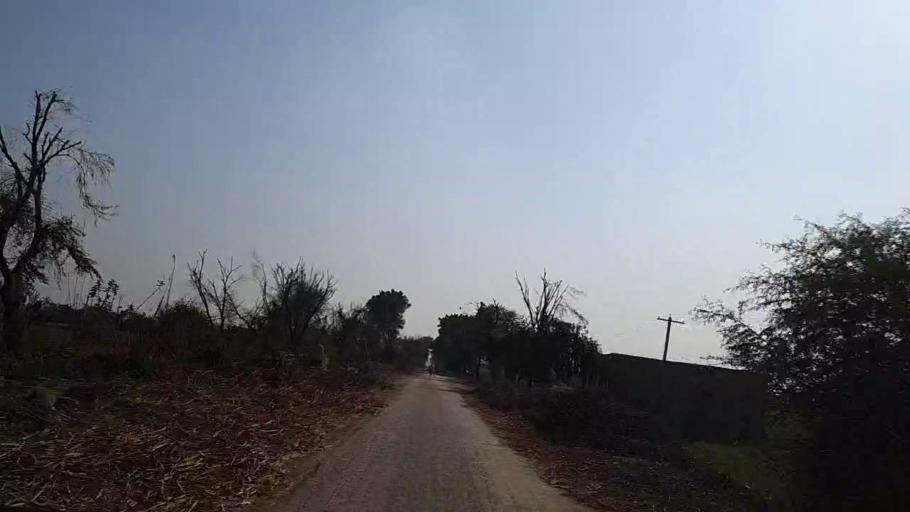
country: PK
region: Sindh
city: Sakrand
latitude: 26.0755
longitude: 68.2899
